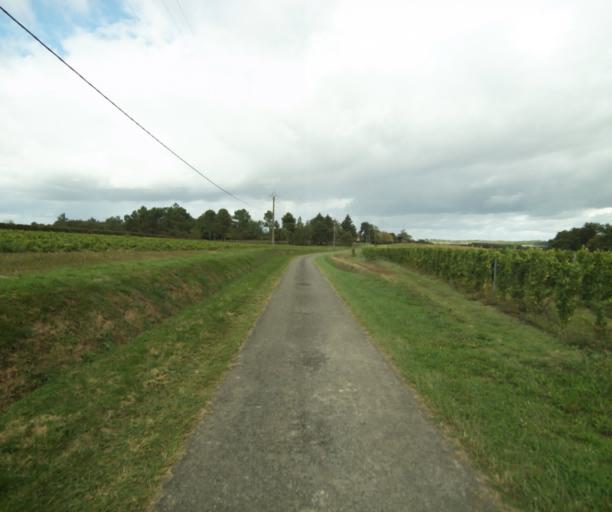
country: FR
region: Midi-Pyrenees
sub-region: Departement du Gers
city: Cazaubon
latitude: 43.8646
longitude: -0.0380
